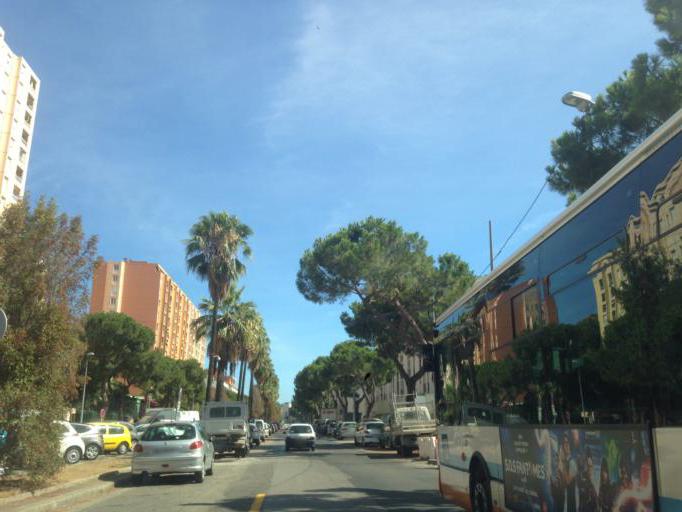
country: FR
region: Provence-Alpes-Cote d'Azur
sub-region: Departement des Alpes-Maritimes
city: Saint-Laurent-du-Var
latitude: 43.6756
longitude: 7.2068
